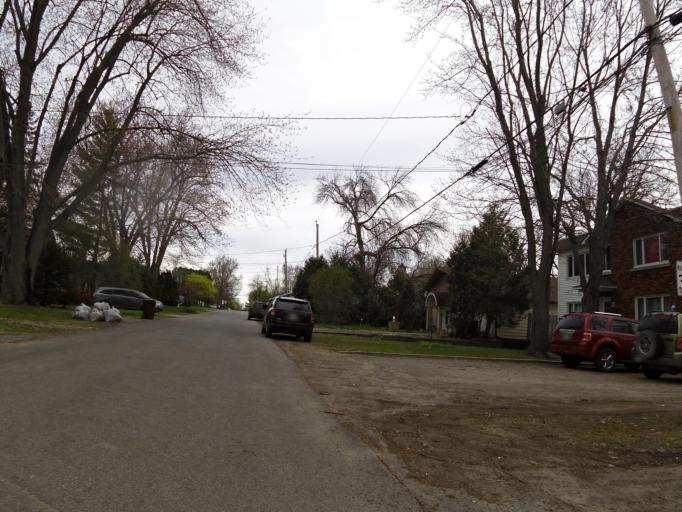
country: CA
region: Quebec
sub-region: Laurentides
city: Deux-Montagnes
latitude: 45.5366
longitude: -73.8949
